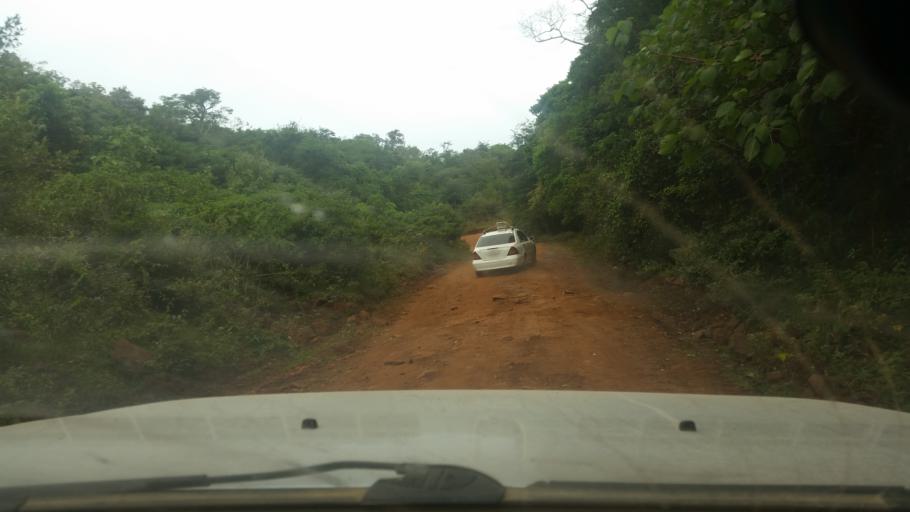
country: PY
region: Guaira
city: Independencia
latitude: -25.8169
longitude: -56.2756
